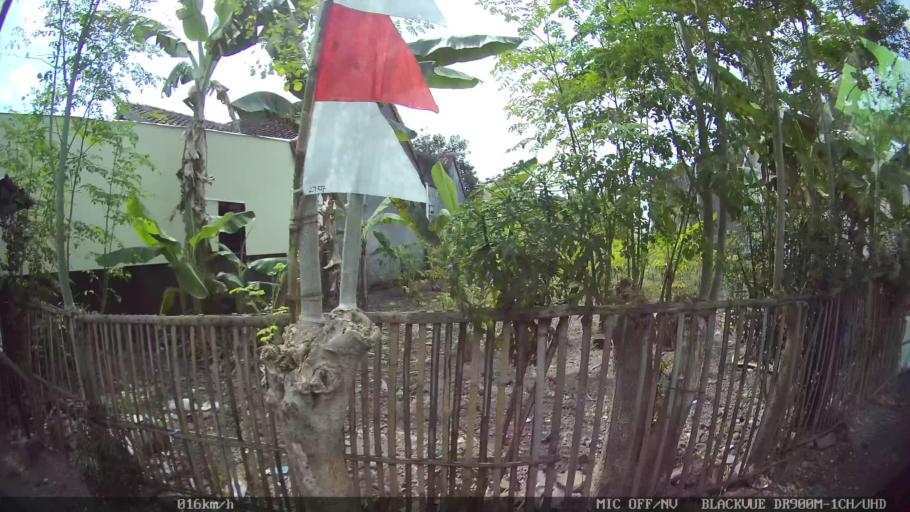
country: ID
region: Daerah Istimewa Yogyakarta
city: Kasihan
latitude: -7.8237
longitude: 110.3388
